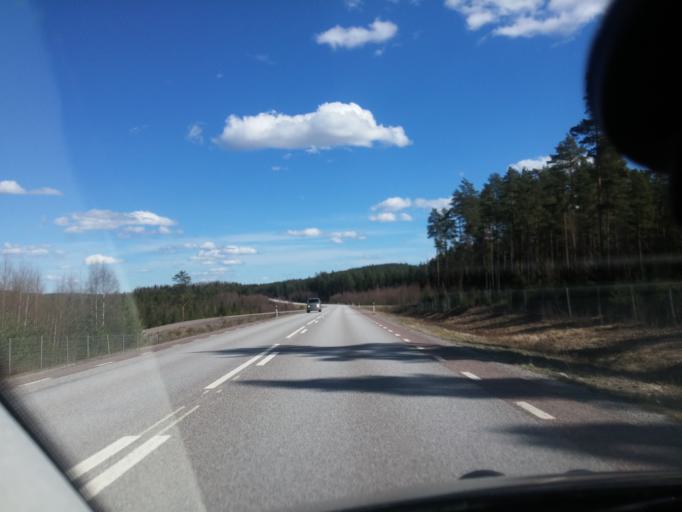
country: SE
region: Dalarna
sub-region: Faluns Kommun
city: Falun
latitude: 60.6762
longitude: 15.6632
